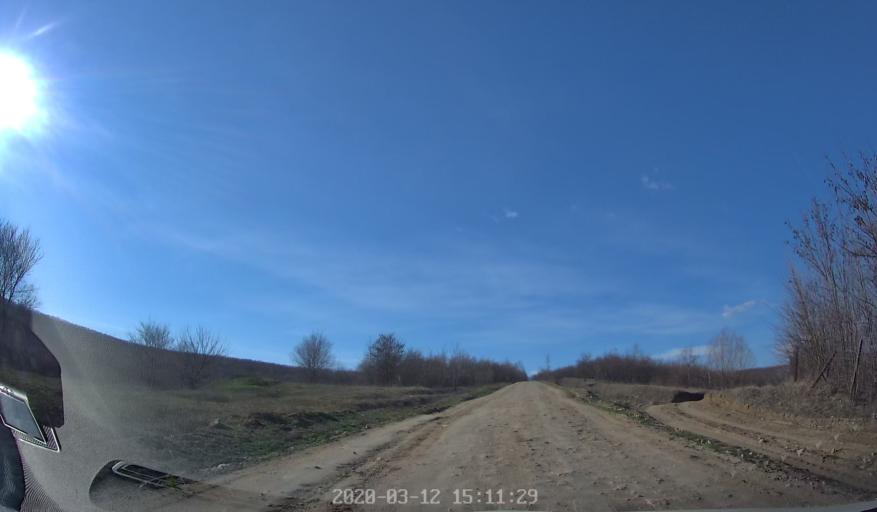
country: MD
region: Chisinau
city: Ciorescu
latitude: 47.2269
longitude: 28.9756
